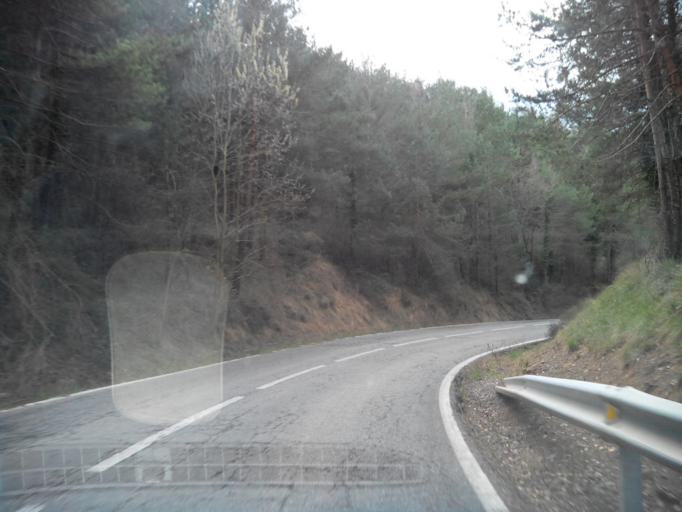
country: ES
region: Catalonia
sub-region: Provincia de Barcelona
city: Olost
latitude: 41.9682
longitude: 2.1369
